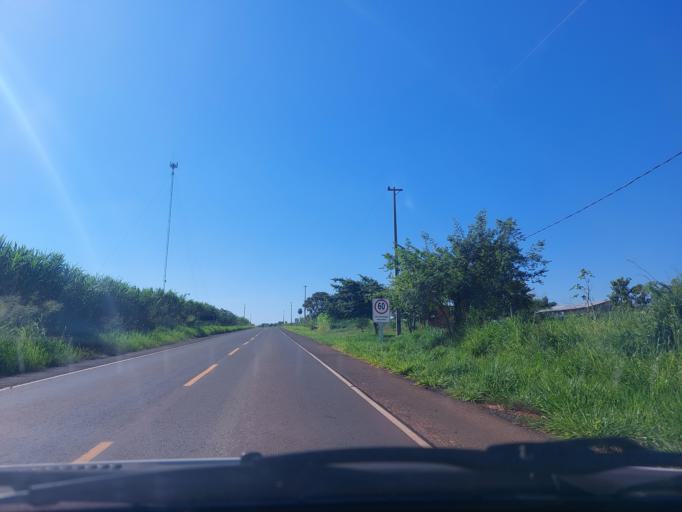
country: PY
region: San Pedro
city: Guayaybi
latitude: -24.3175
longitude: -56.1720
